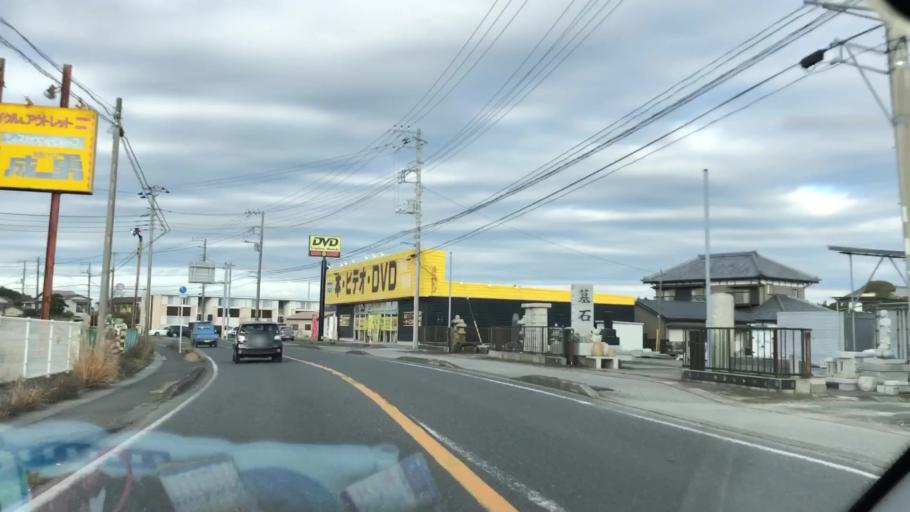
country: JP
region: Chiba
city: Tateyama
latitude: 34.9993
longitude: 139.9063
